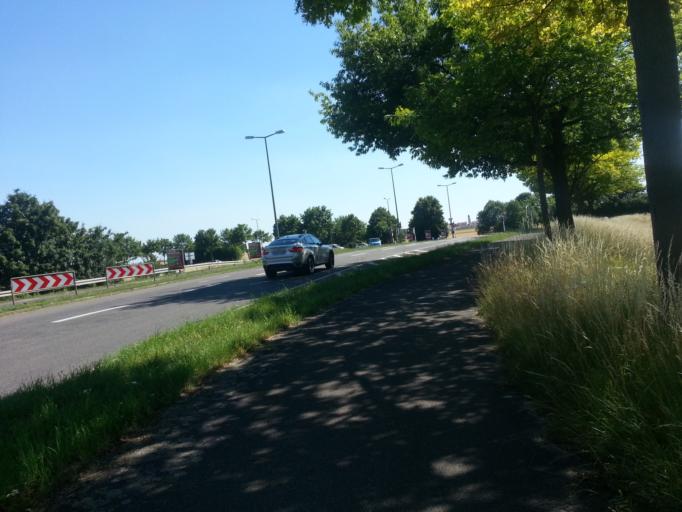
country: DE
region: Hesse
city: Viernheim
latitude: 49.5103
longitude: 8.5566
